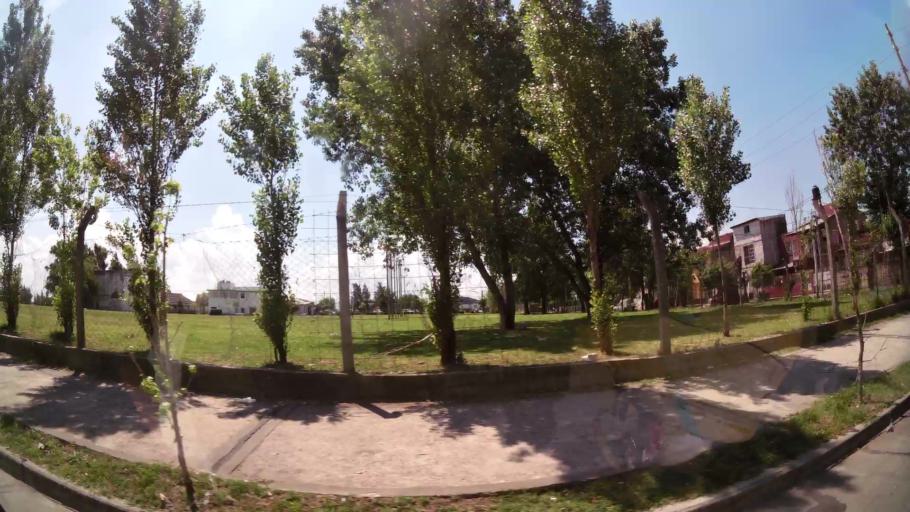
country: AR
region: Buenos Aires
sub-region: Partido de Tigre
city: Tigre
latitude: -34.4567
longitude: -58.5804
